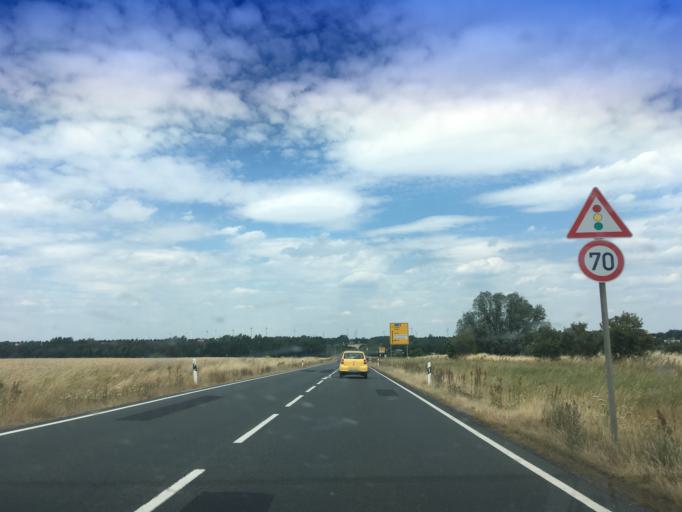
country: DE
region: Saxony
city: Goerlitz
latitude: 51.1680
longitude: 14.9584
